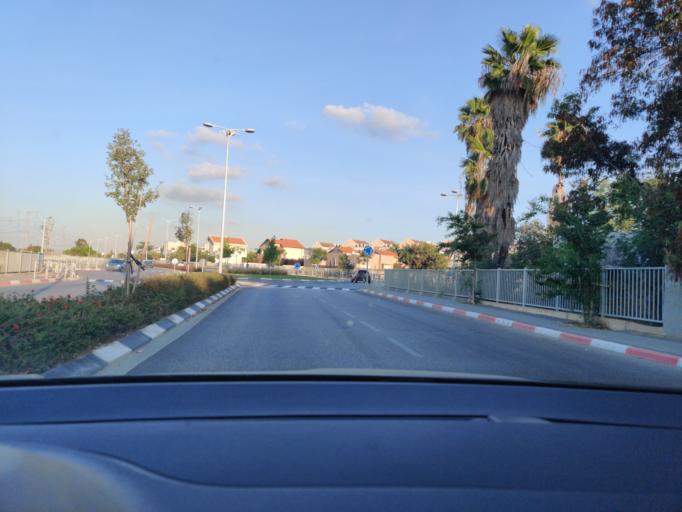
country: IL
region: Central District
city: Elyakhin
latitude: 32.4378
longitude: 34.9399
